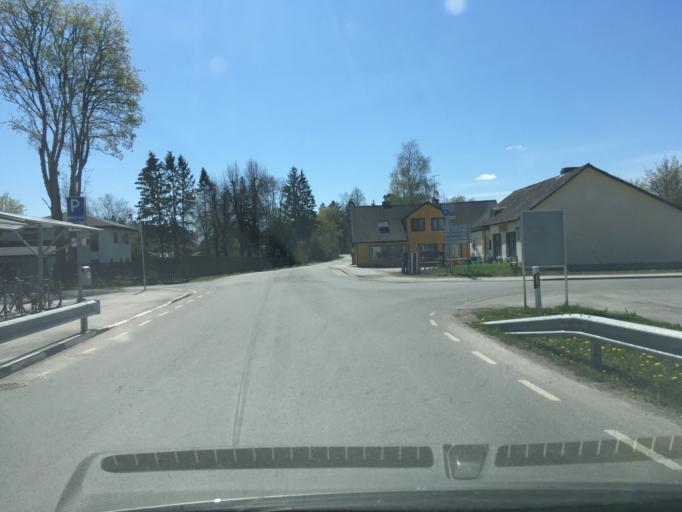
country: EE
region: Harju
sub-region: Raasiku vald
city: Arukula
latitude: 59.3720
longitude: 25.0791
